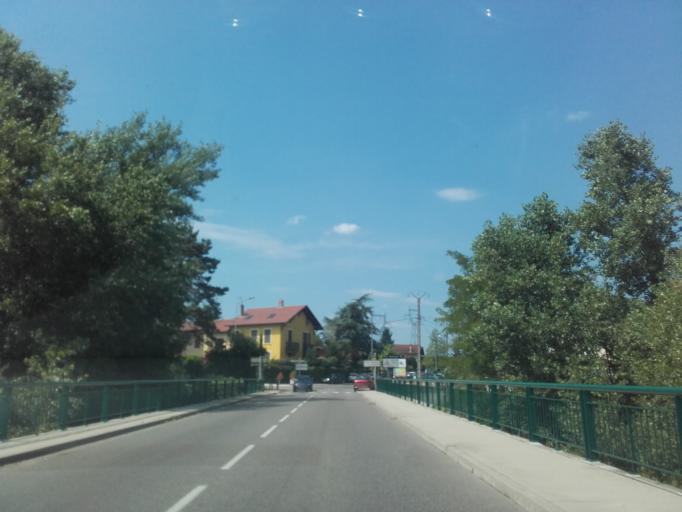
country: FR
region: Rhone-Alpes
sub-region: Departement de l'Ain
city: Saint-Jean-de-Niost
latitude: 45.8169
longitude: 5.2125
